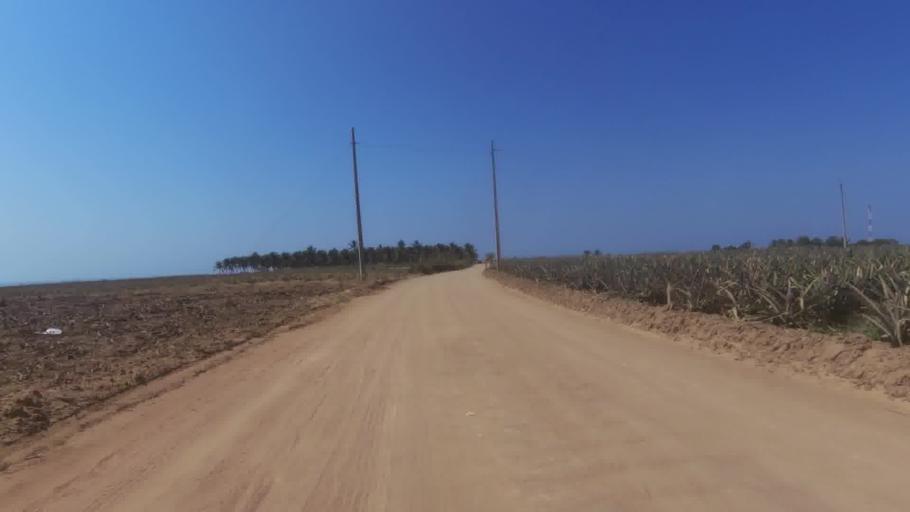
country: BR
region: Espirito Santo
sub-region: Marataizes
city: Marataizes
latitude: -21.1071
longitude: -40.8608
